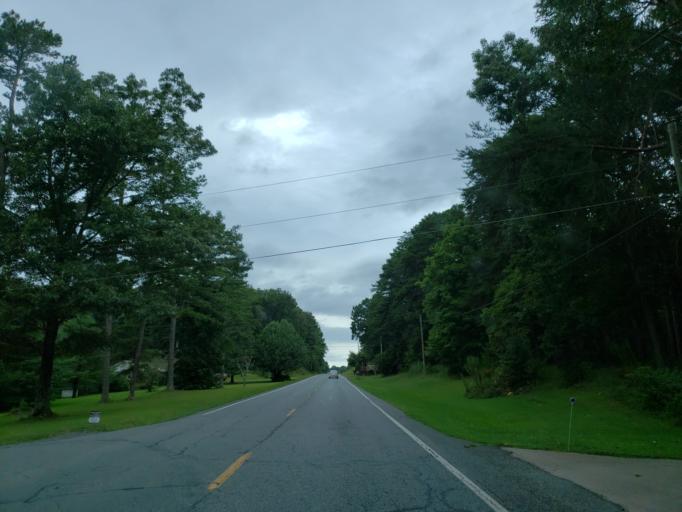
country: US
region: Georgia
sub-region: Gilmer County
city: Ellijay
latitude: 34.6409
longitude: -84.5384
